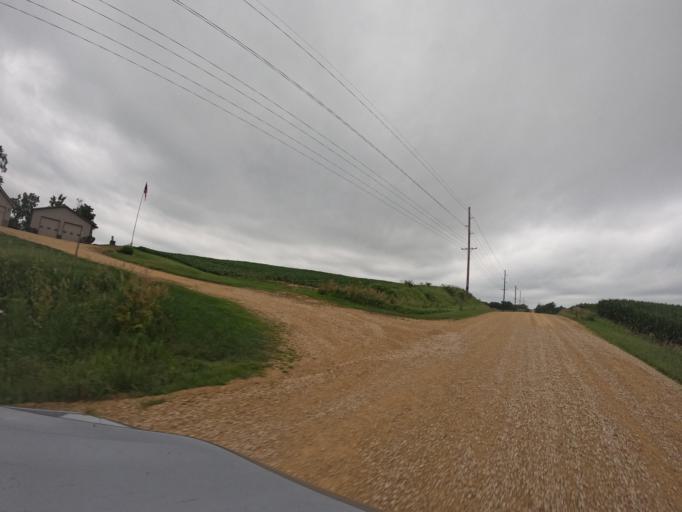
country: US
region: Iowa
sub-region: Jackson County
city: Maquoketa
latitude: 41.9381
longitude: -90.6357
